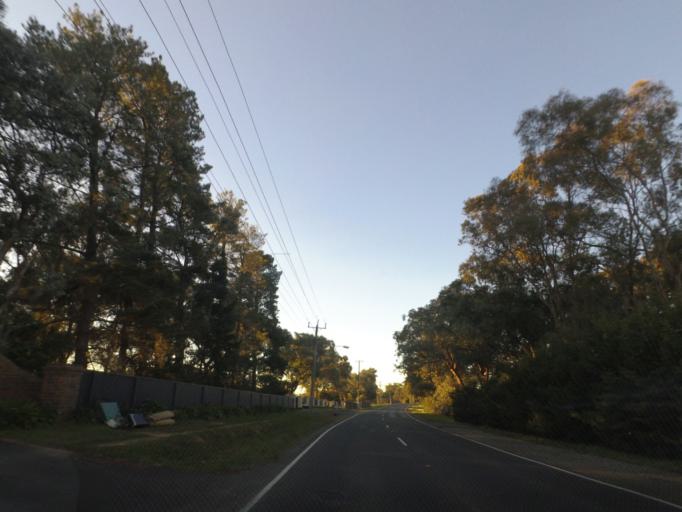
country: AU
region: Victoria
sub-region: Manningham
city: Park Orchards
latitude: -37.7592
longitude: 145.1963
